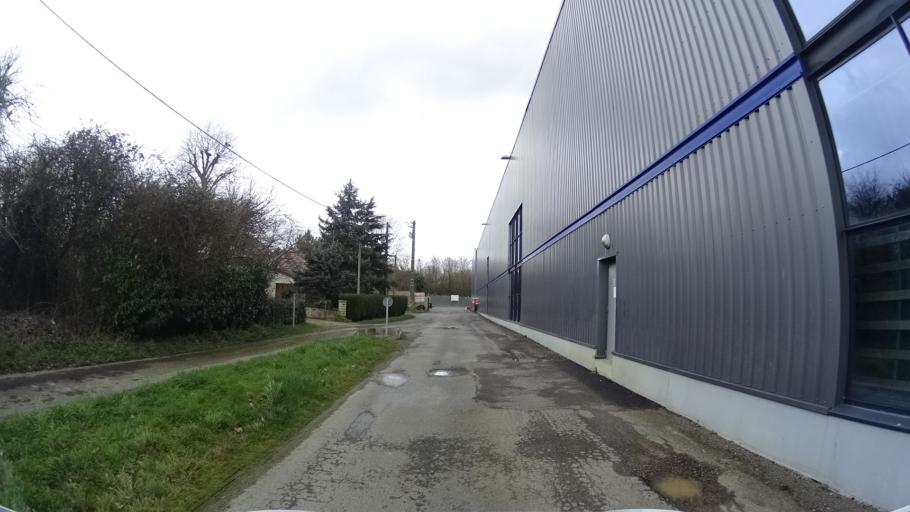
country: FR
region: Brittany
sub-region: Departement d'Ille-et-Vilaine
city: Saint-Gilles
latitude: 48.1576
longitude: -1.8364
